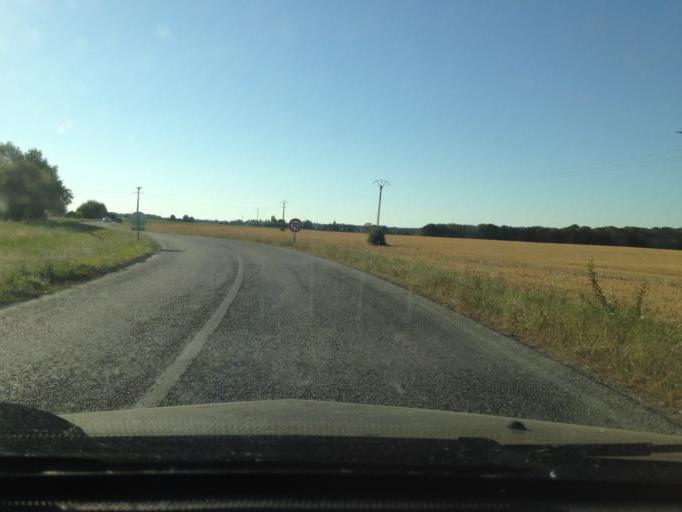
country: FR
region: Ile-de-France
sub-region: Departement des Yvelines
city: Magny-les-Hameaux
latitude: 48.7351
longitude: 2.0713
